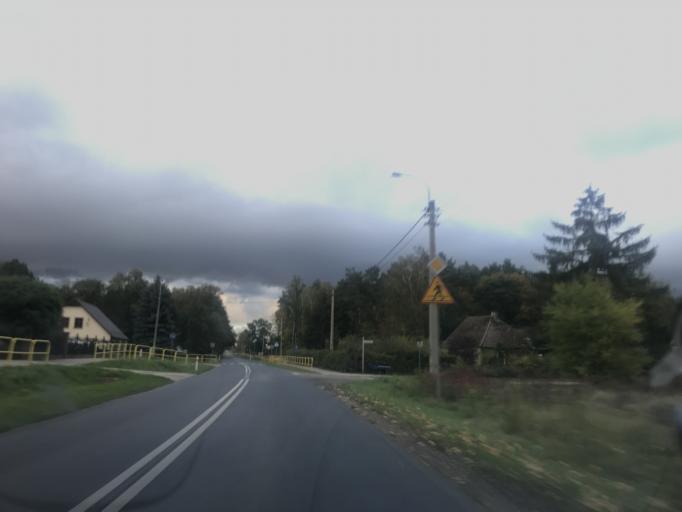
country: PL
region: West Pomeranian Voivodeship
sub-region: Powiat walecki
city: Tuczno
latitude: 53.2055
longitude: 16.1659
